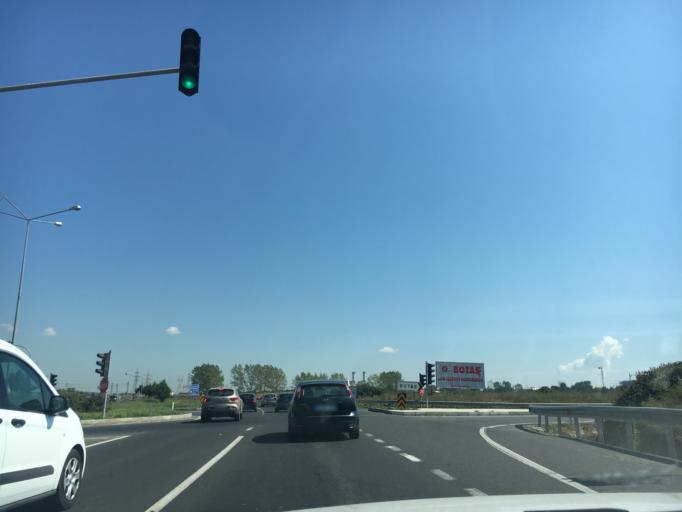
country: TR
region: Tekirdag
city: Marmara Ereglisi
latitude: 40.9880
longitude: 27.9716
